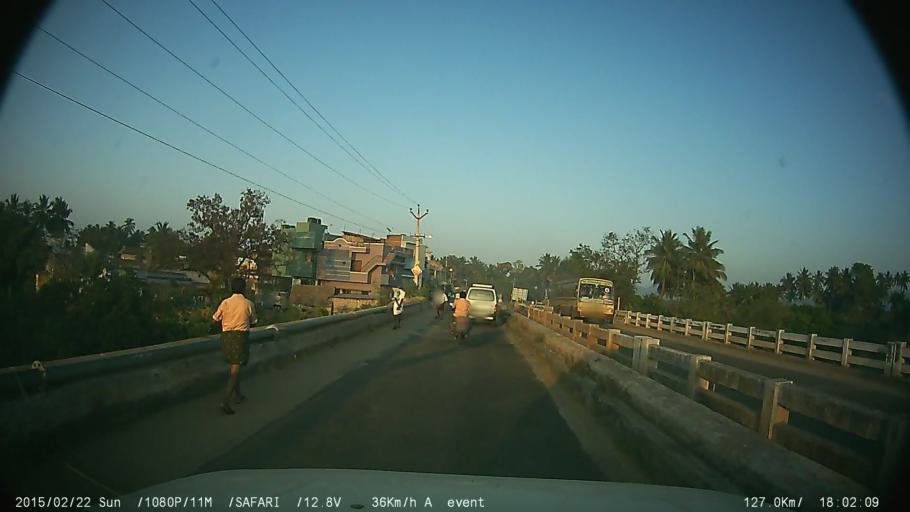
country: IN
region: Tamil Nadu
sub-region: Theni
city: Uttamapalaiyam
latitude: 9.8066
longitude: 77.3377
